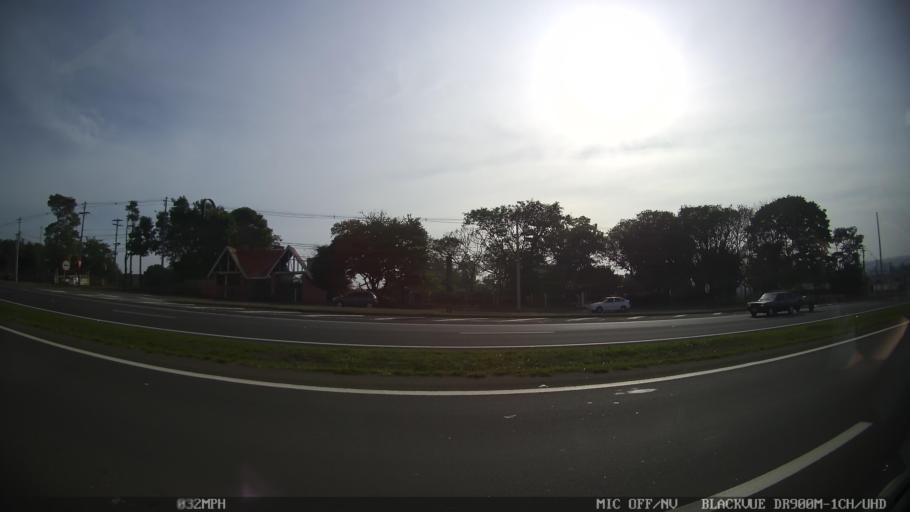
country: BR
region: Sao Paulo
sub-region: Piracicaba
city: Piracicaba
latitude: -22.6810
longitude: -47.6982
